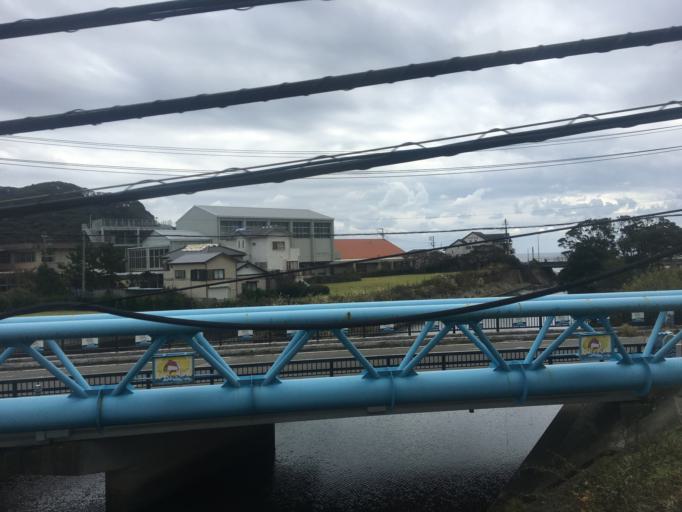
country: JP
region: Chiba
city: Kawaguchi
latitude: 35.1291
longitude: 140.1927
